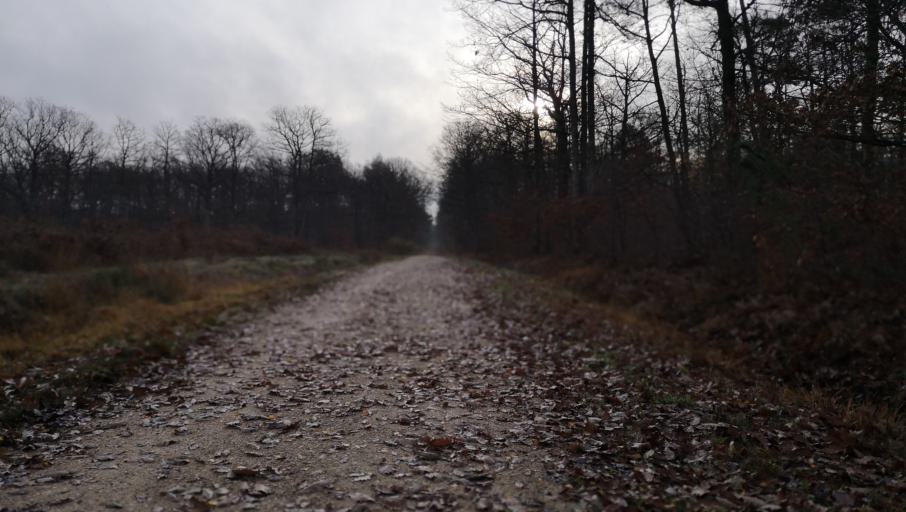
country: FR
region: Centre
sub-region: Departement du Loiret
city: Chanteau
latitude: 47.9463
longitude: 1.9670
